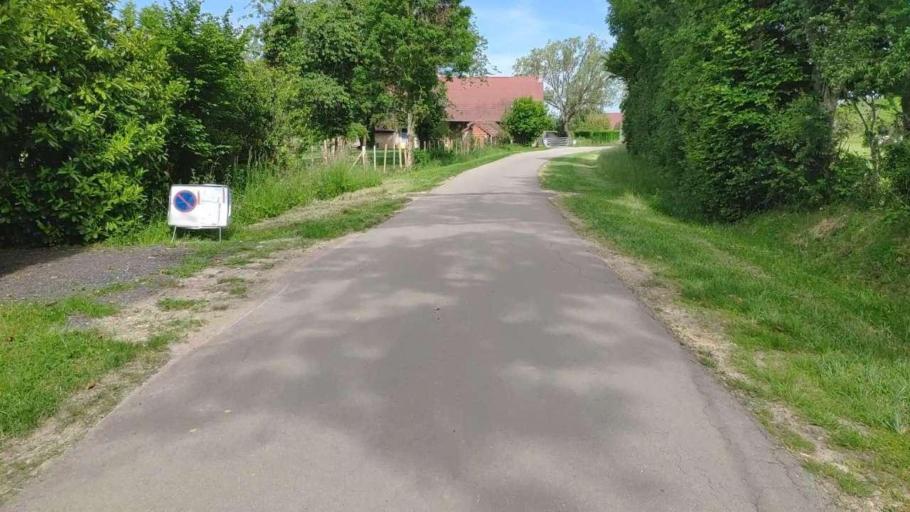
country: FR
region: Franche-Comte
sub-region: Departement du Jura
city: Bletterans
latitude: 46.7078
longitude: 5.4477
